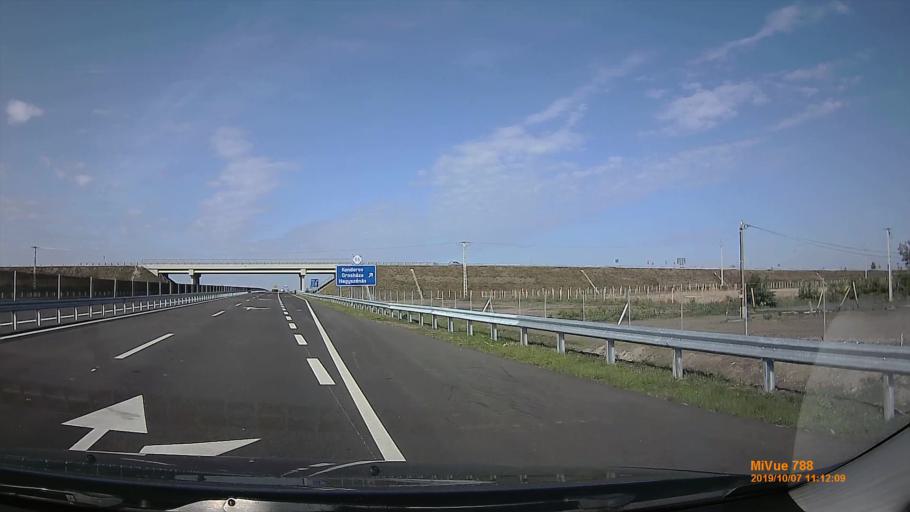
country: HU
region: Bekes
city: Kondoros
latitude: 46.7390
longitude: 20.7855
